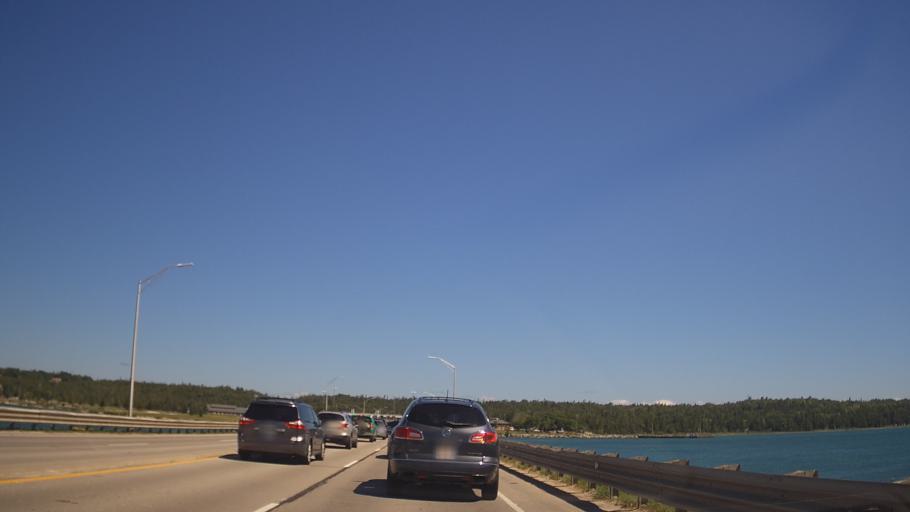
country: US
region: Michigan
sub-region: Mackinac County
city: Saint Ignace
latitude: 45.8425
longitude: -84.7240
